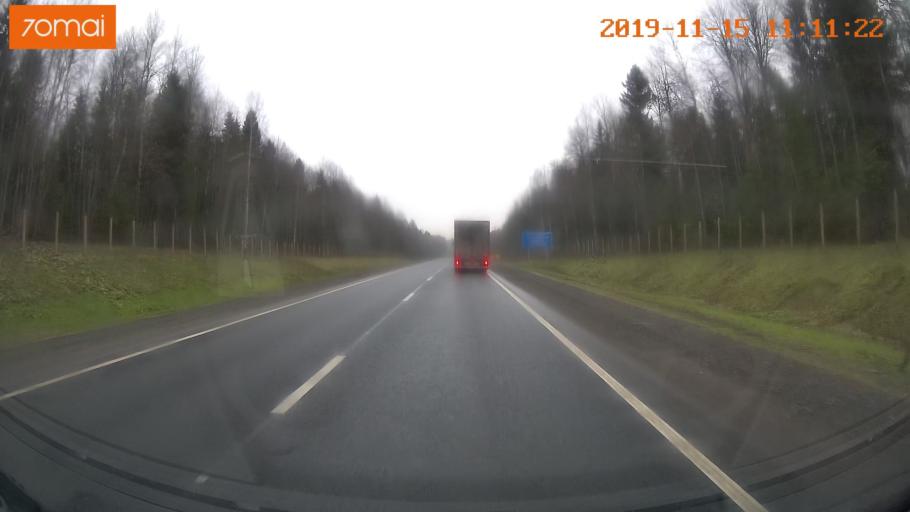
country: RU
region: Vologda
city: Chebsara
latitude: 59.1213
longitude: 39.1419
